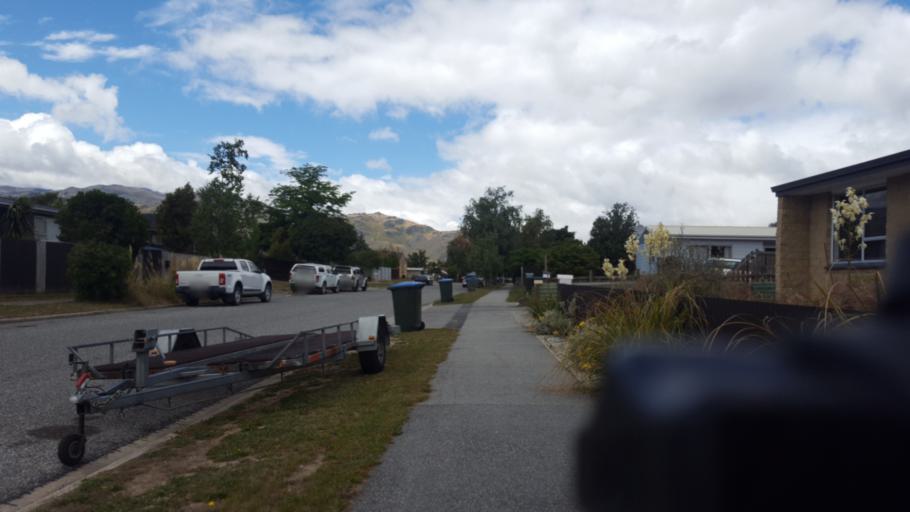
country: NZ
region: Otago
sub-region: Queenstown-Lakes District
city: Wanaka
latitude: -45.0413
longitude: 169.1821
